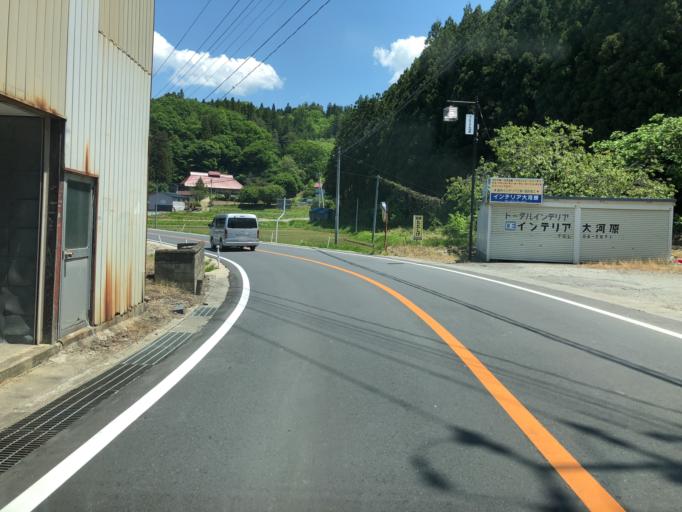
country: JP
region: Fukushima
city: Funehikimachi-funehiki
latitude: 37.4970
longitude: 140.5917
